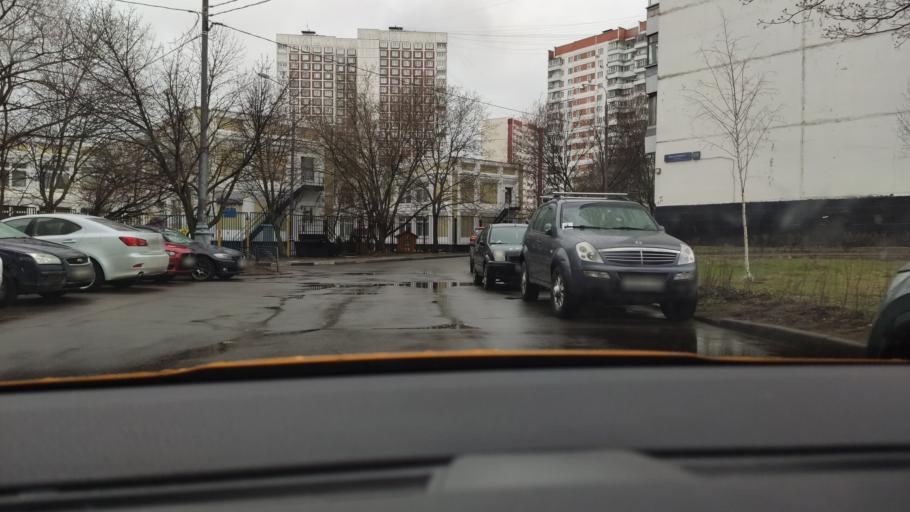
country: RU
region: Moscow
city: Strogino
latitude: 55.8493
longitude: 37.4152
